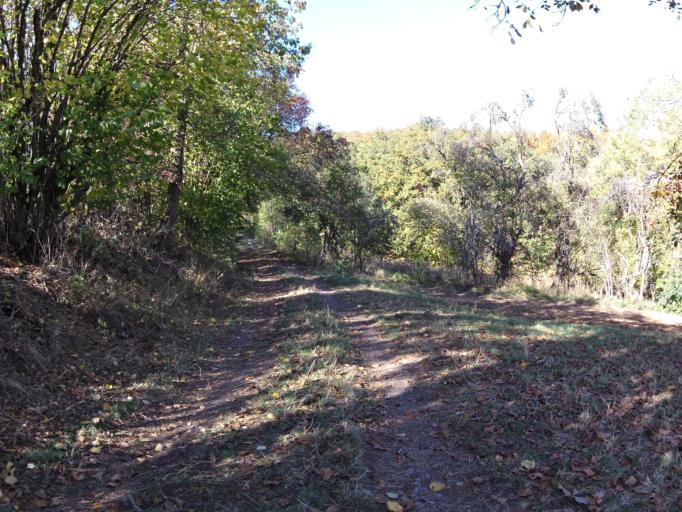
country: DE
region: Bavaria
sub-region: Regierungsbezirk Unterfranken
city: Eibelstadt
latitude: 49.7217
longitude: 9.9835
